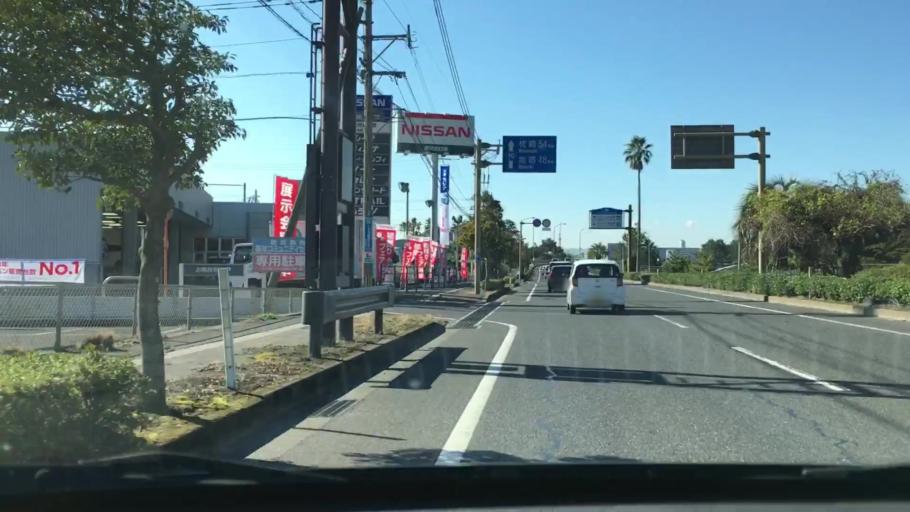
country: JP
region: Kagoshima
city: Kagoshima-shi
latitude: 31.6053
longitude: 130.5720
